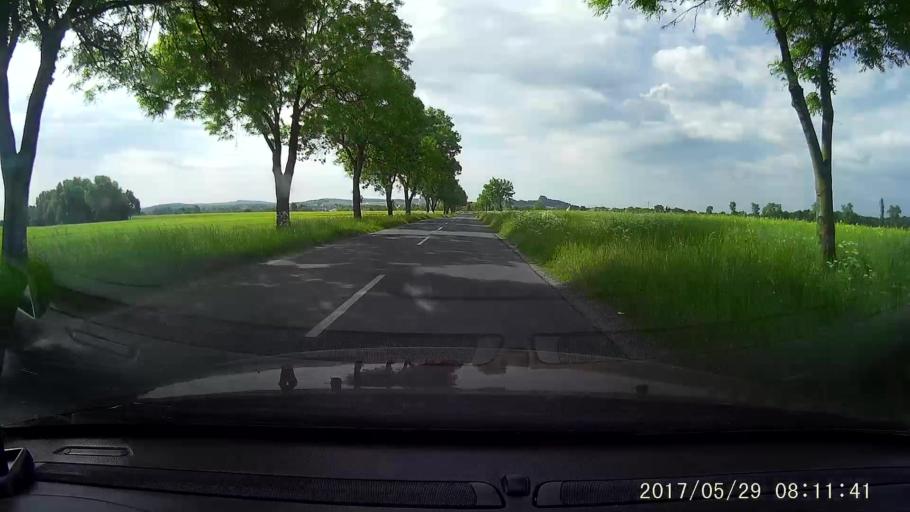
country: PL
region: Lower Silesian Voivodeship
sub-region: Powiat zlotoryjski
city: Zlotoryja
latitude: 51.1391
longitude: 15.9057
